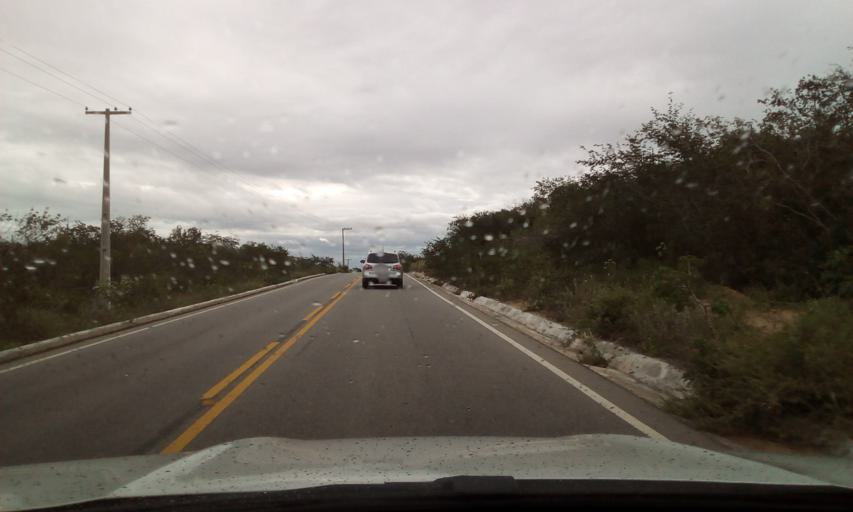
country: BR
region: Paraiba
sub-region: Picui
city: Picui
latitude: -6.5730
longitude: -36.2685
